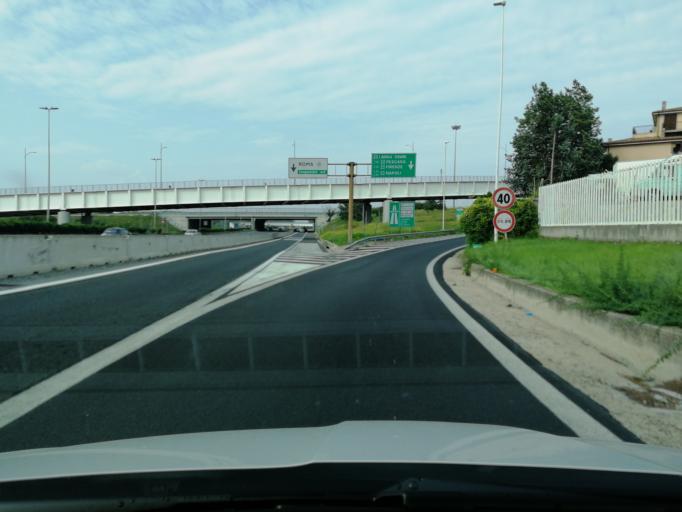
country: IT
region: Latium
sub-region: Citta metropolitana di Roma Capitale
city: Setteville
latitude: 41.9187
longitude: 12.6131
